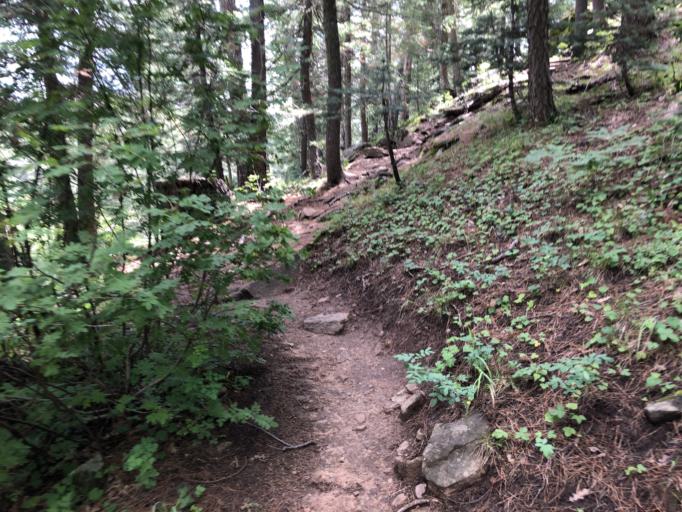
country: US
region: Arizona
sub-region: Gila County
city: Star Valley
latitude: 34.3391
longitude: -110.9532
